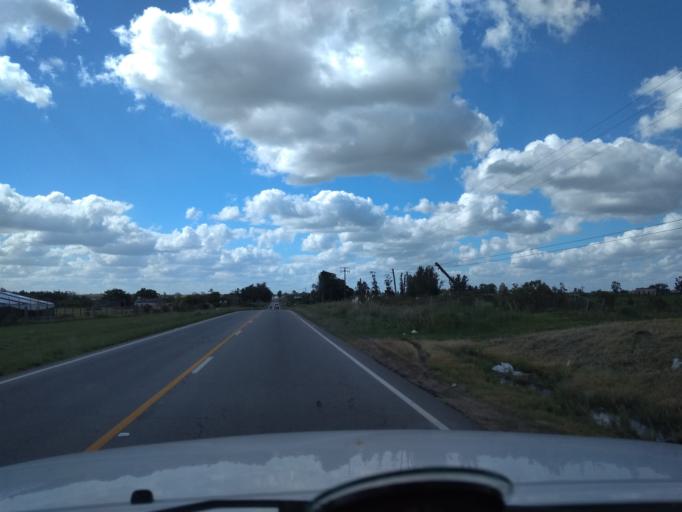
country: UY
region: Canelones
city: Joaquin Suarez
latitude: -34.7024
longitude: -56.0574
